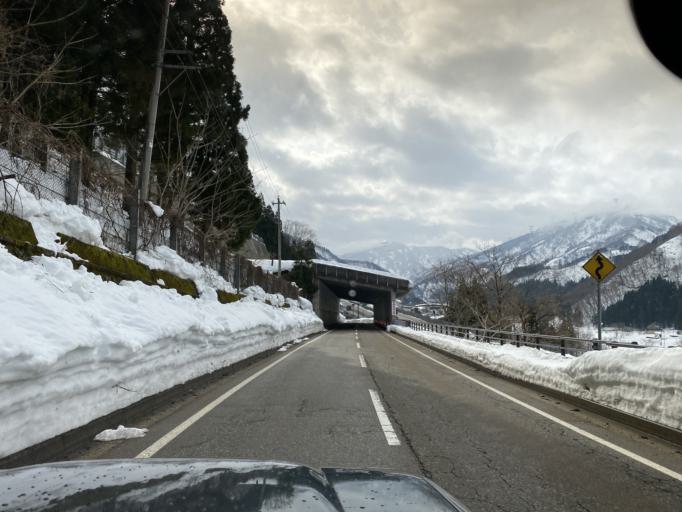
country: JP
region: Toyama
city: Fukumitsu
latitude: 36.3972
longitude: 136.8799
